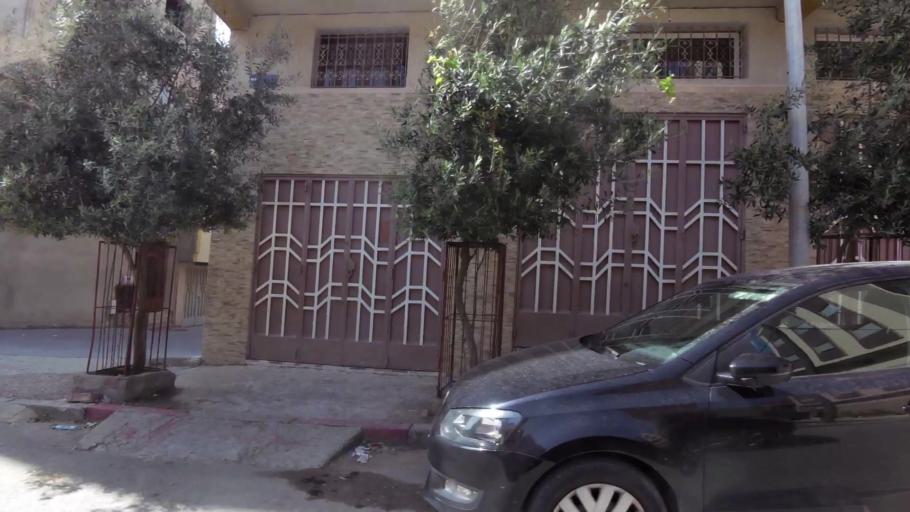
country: MA
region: Tanger-Tetouan
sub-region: Tanger-Assilah
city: Tangier
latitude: 35.7313
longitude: -5.8055
